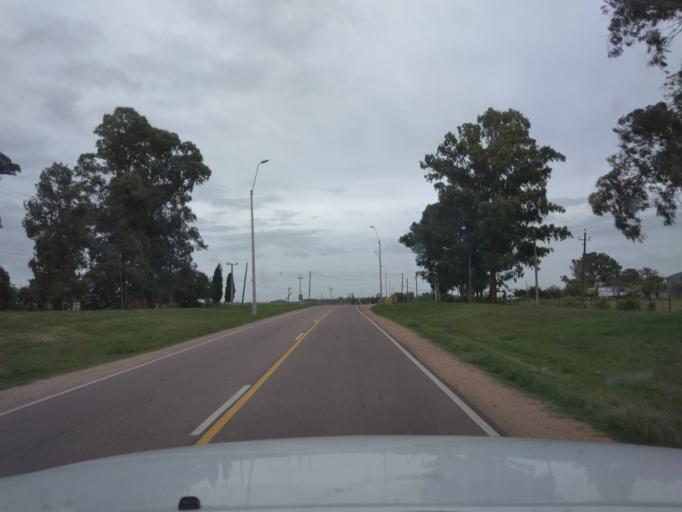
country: UY
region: Canelones
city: Tala
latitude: -34.3597
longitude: -55.7745
